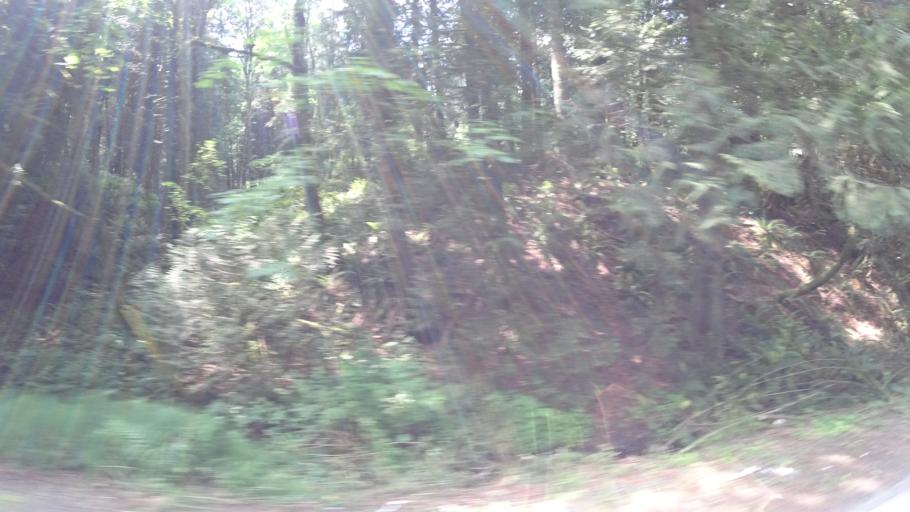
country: US
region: Oregon
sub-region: Clackamas County
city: Happy Valley
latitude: 45.4691
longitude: -122.5100
